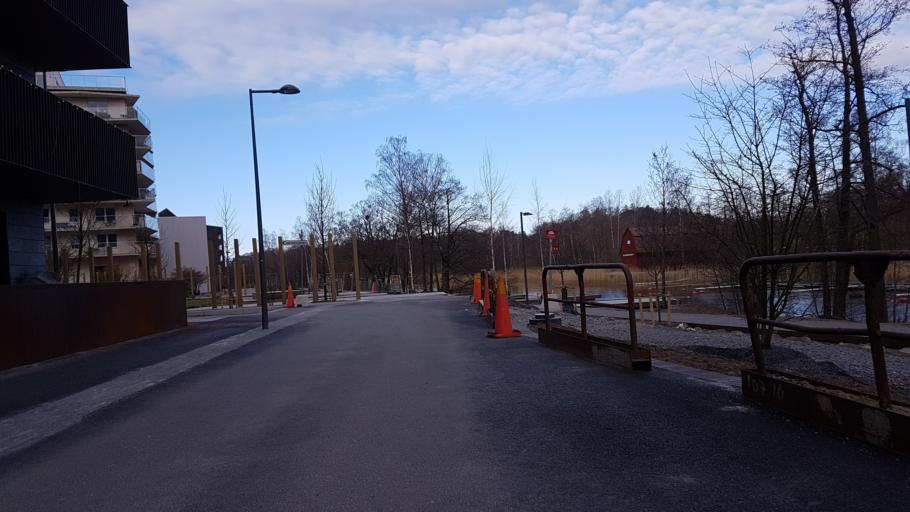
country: SE
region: Stockholm
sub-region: Stockholms Kommun
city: OEstermalm
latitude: 59.3602
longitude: 18.0929
